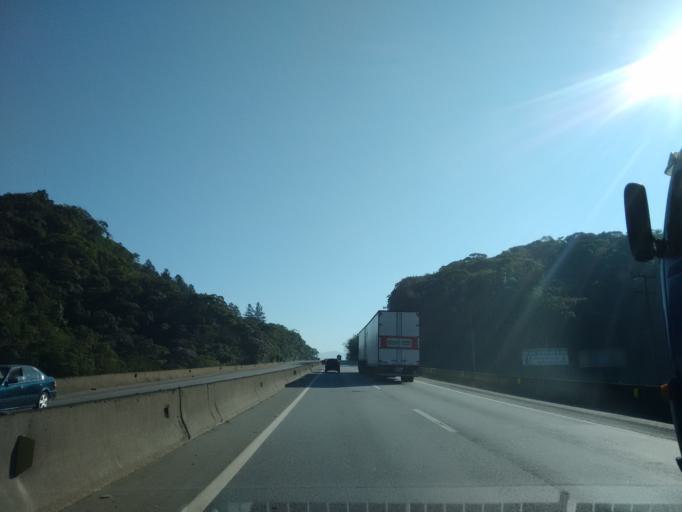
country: BR
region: Santa Catarina
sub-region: Joinville
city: Joinville
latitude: -26.2293
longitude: -48.9166
